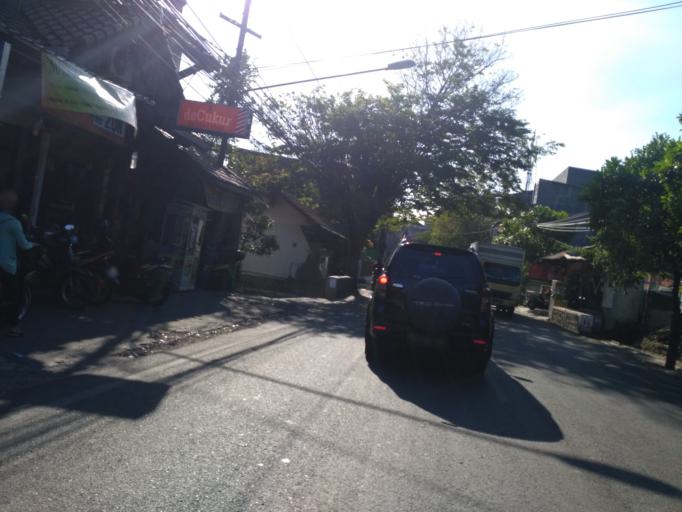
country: ID
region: East Java
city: Malang
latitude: -7.9559
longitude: 112.6120
